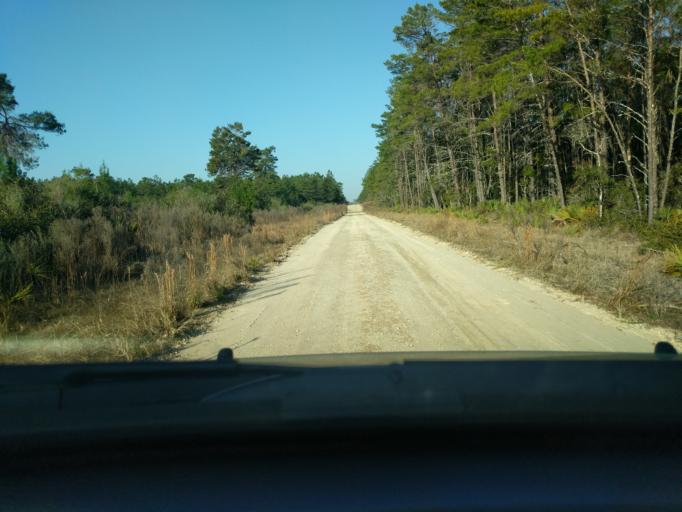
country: US
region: Florida
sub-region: Lake County
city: Astor
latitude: 29.2260
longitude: -81.7591
